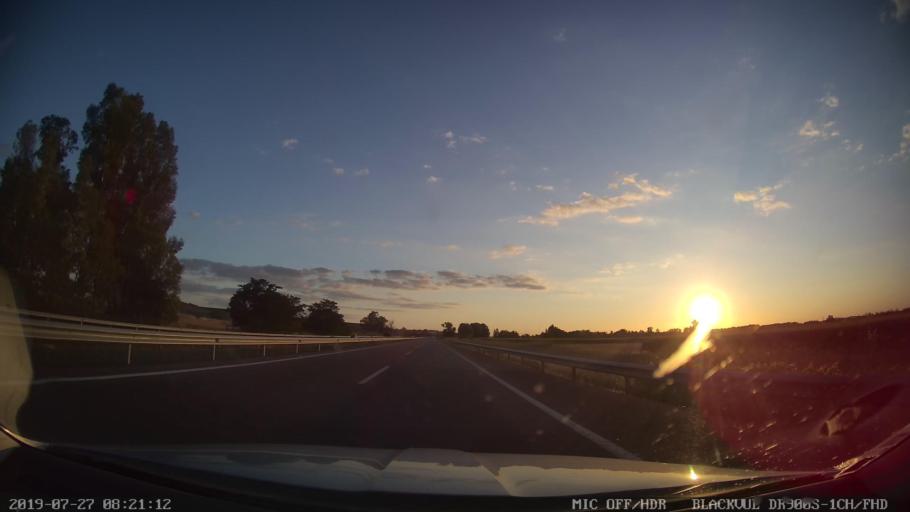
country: ES
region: Extremadura
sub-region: Provincia de Badajoz
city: Torremayor
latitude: 38.8648
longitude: -6.5200
